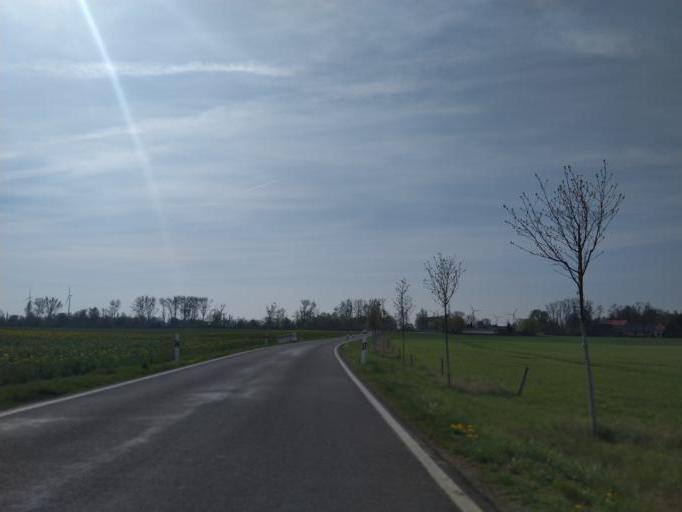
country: DE
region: Brandenburg
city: Wriezen
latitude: 52.7280
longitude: 14.1697
